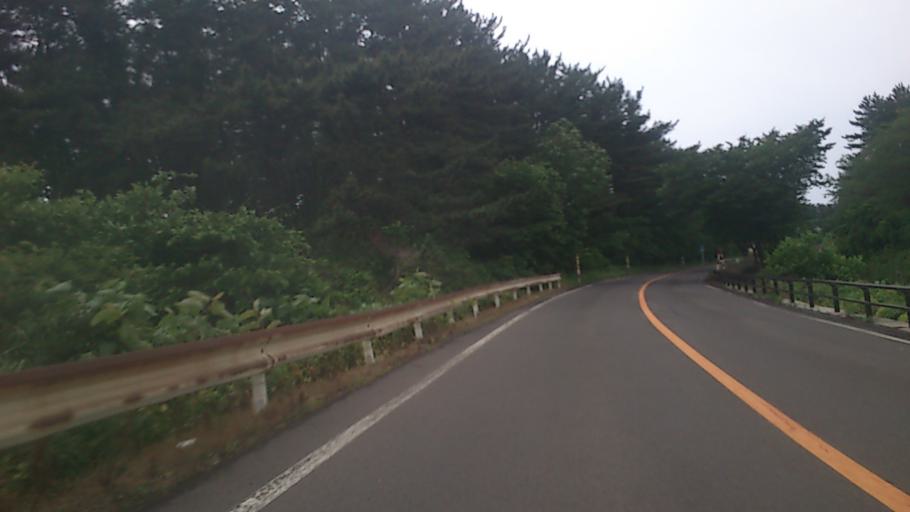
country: JP
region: Akita
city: Noshiromachi
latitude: 40.3874
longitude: 139.9857
